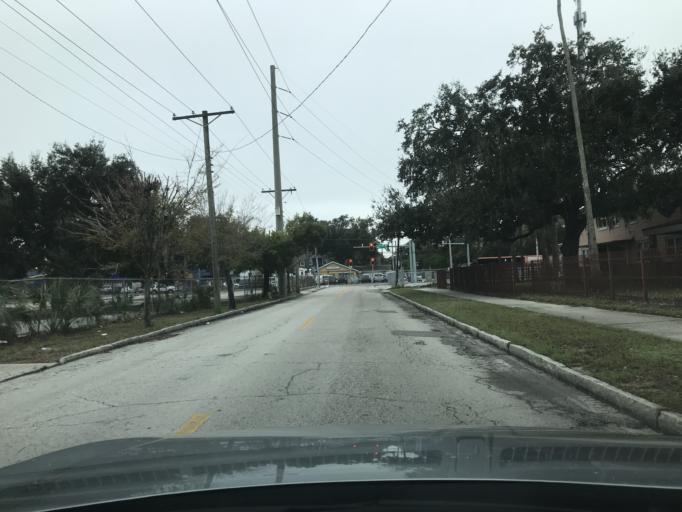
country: US
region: Florida
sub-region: Hillsborough County
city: Tampa
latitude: 27.9779
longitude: -82.4584
